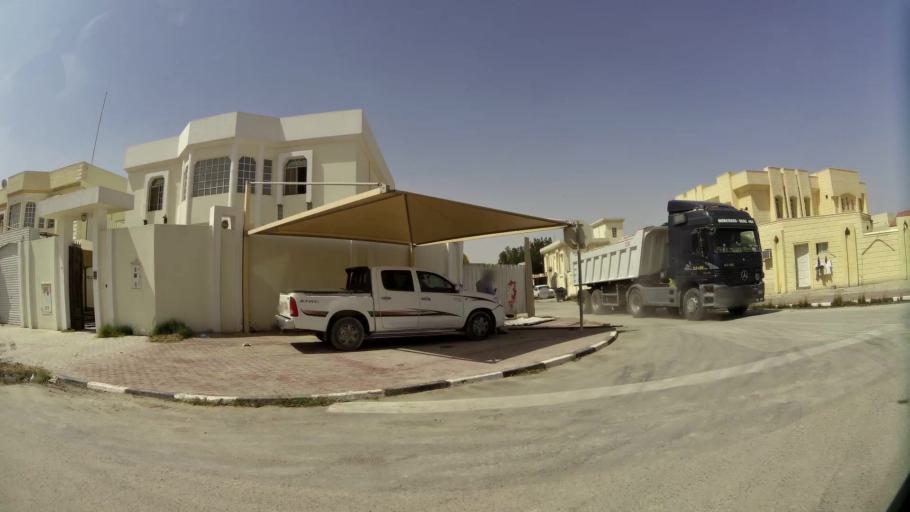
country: QA
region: Baladiyat Umm Salal
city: Umm Salal Muhammad
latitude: 25.3801
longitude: 51.4267
